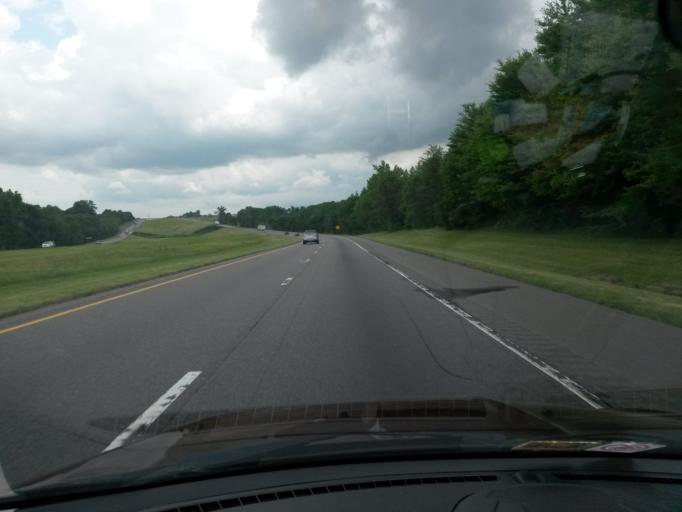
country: US
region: North Carolina
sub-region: Iredell County
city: Statesville
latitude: 35.9334
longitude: -80.8558
